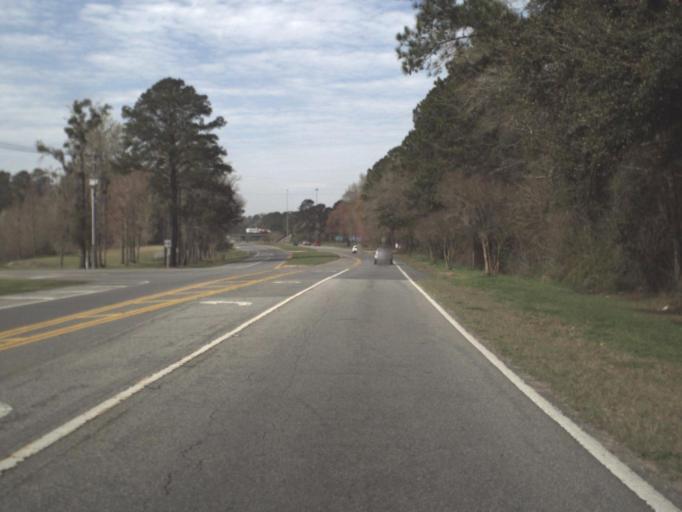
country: US
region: Florida
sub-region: Leon County
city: Tallahassee
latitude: 30.4875
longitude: -84.1513
